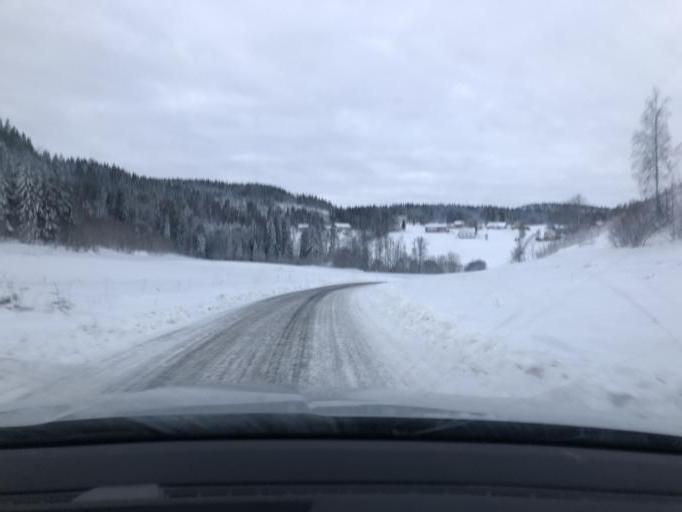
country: SE
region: Vaesternorrland
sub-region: Kramfors Kommun
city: Nordingra
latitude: 62.9101
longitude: 18.2373
